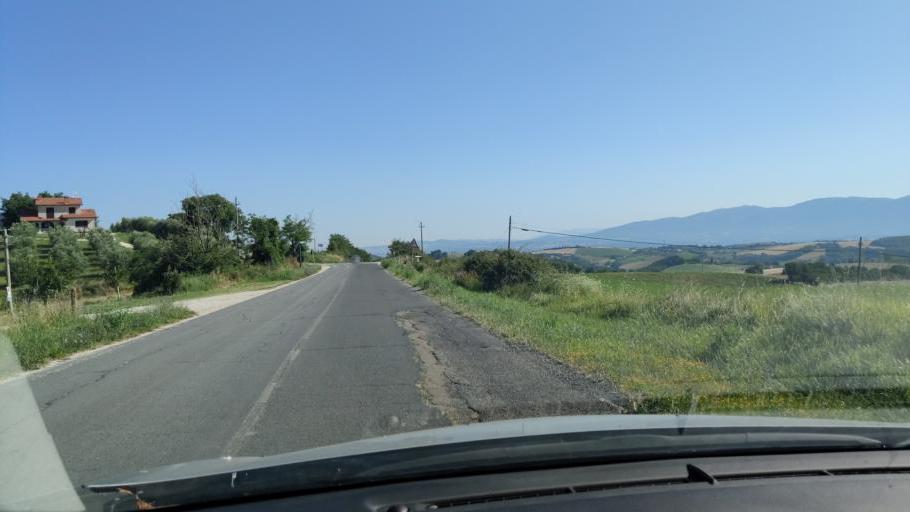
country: IT
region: Umbria
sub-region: Provincia di Terni
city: Avigliano Umbro
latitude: 42.6737
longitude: 12.4403
